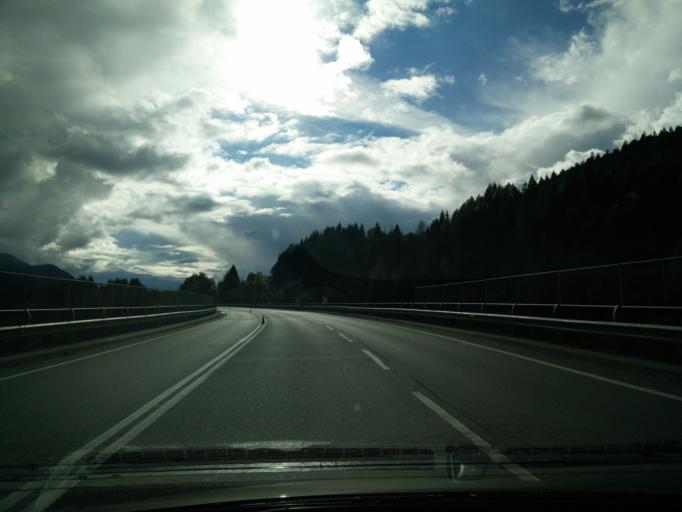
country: IT
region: Veneto
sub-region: Provincia di Belluno
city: Lozzo di Cadore
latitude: 46.4815
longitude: 12.4424
